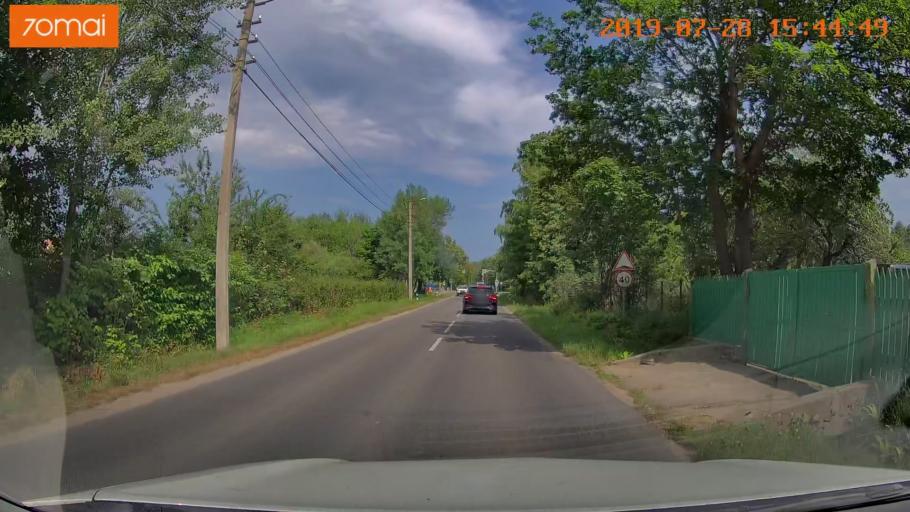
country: RU
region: Kaliningrad
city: Donskoye
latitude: 54.9408
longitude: 20.0345
